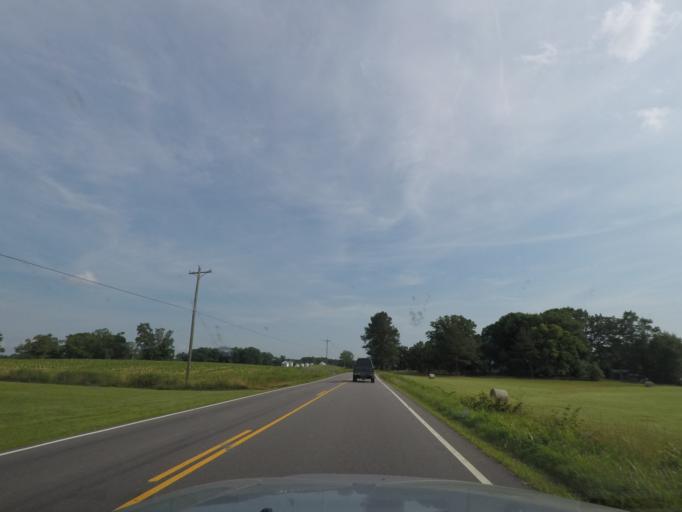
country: US
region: Virginia
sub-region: Mecklenburg County
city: Chase City
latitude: 36.8290
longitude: -78.5939
